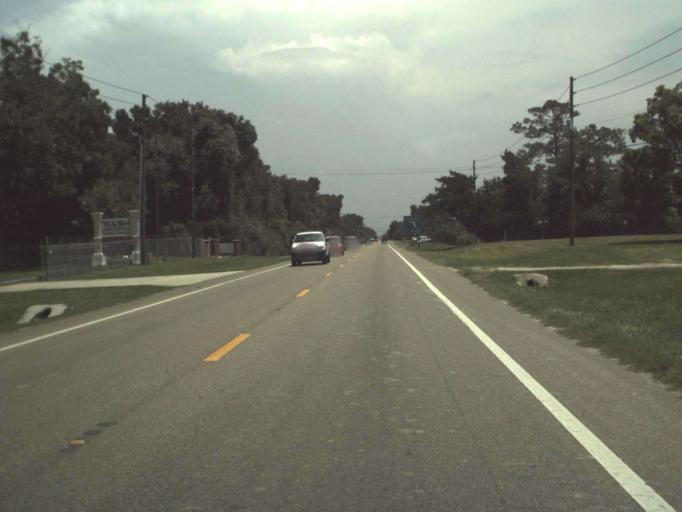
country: US
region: Florida
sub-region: Sumter County
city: Wildwood
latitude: 28.8063
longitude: -82.0456
